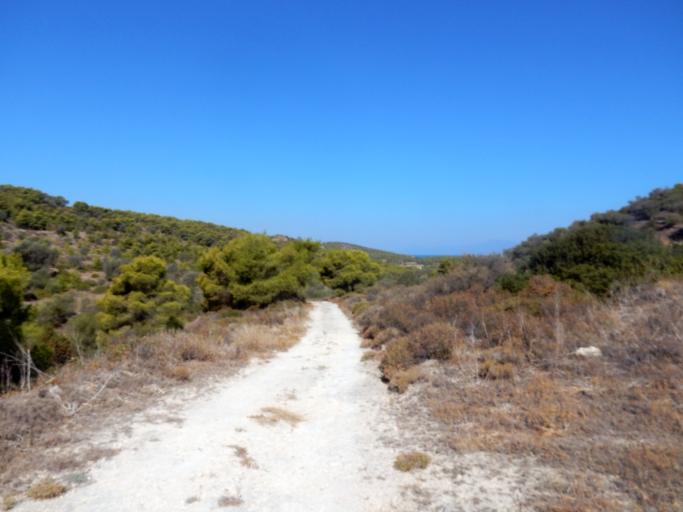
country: GR
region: Attica
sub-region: Nomos Piraios
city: Vathi
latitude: 37.7610
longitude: 23.5425
